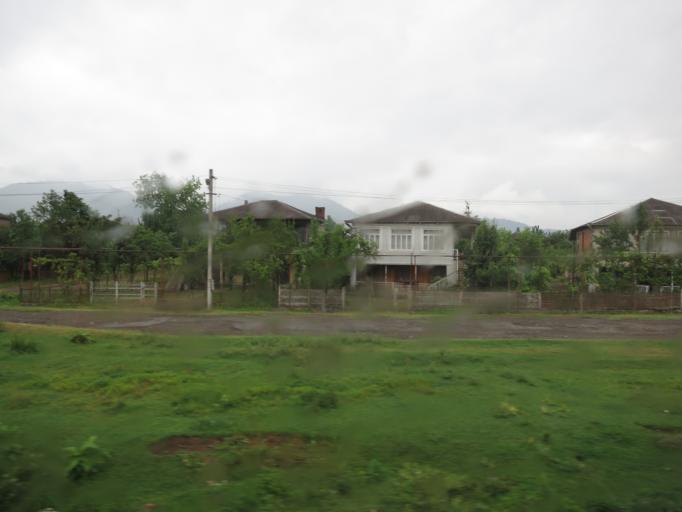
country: GE
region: Guria
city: Lanchkhuti
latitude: 42.0941
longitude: 42.0365
